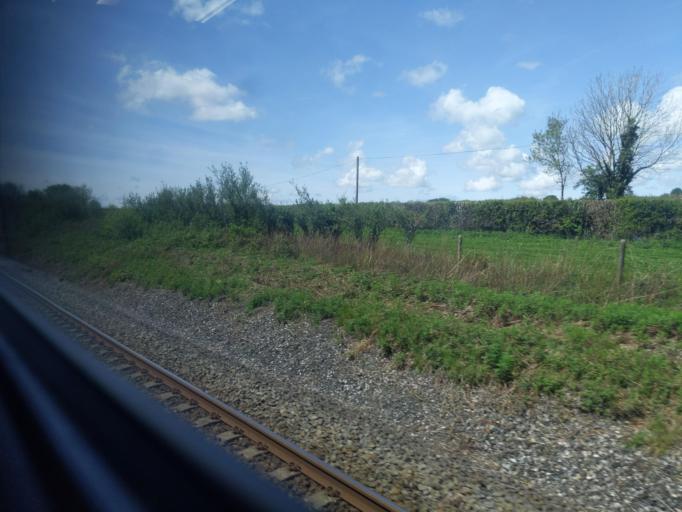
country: GB
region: England
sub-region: Cornwall
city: Liskeard
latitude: 50.4528
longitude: -4.5112
